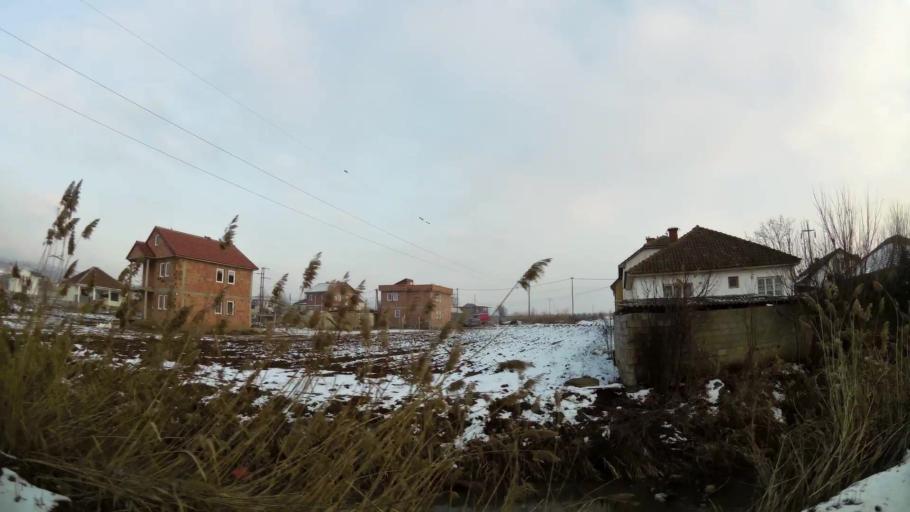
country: MK
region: Aracinovo
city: Arachinovo
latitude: 42.0192
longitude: 21.5598
